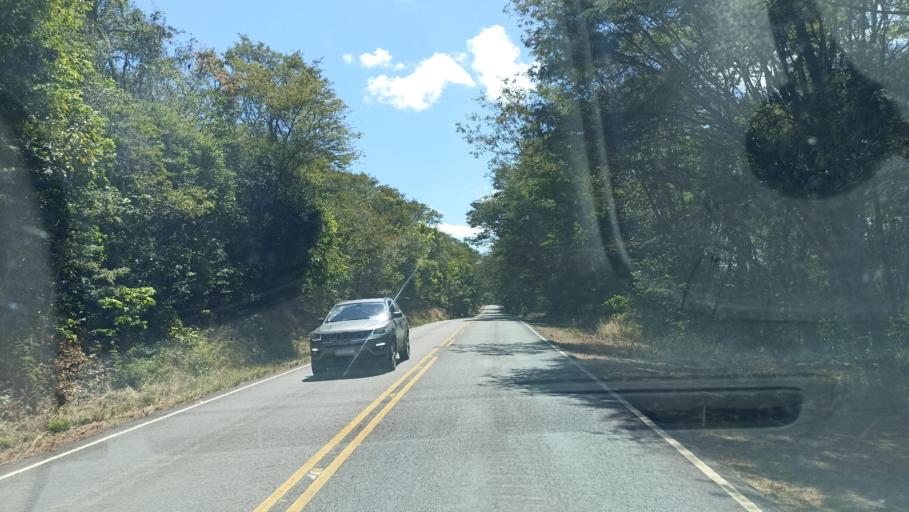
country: BR
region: Bahia
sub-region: Andarai
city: Vera Cruz
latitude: -12.7755
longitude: -41.3300
